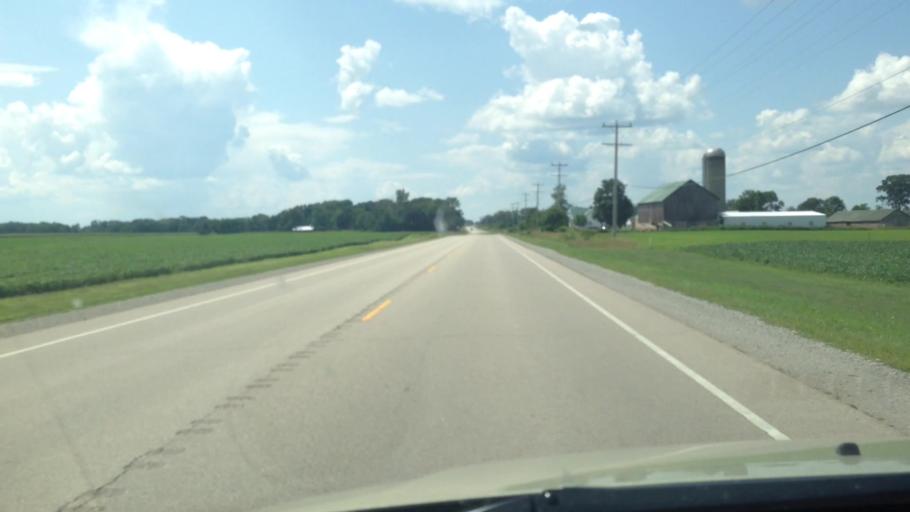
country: US
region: Wisconsin
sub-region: Brown County
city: Pulaski
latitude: 44.6733
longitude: -88.2766
